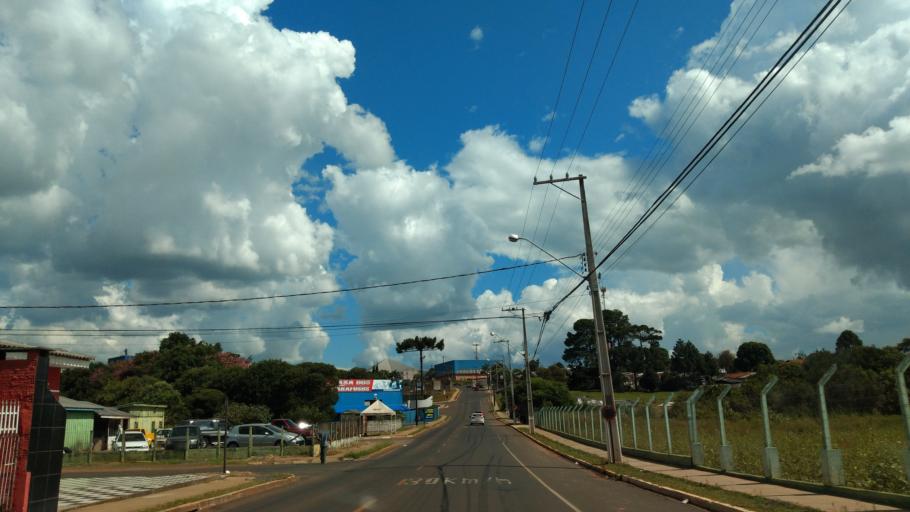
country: BR
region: Parana
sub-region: Guarapuava
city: Guarapuava
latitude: -25.3955
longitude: -51.4931
